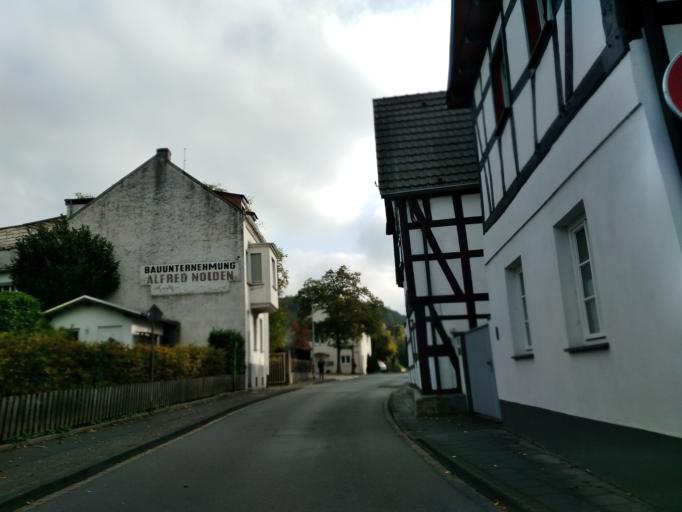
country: DE
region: North Rhine-Westphalia
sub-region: Regierungsbezirk Koln
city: Konigswinter
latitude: 50.6962
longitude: 7.1877
